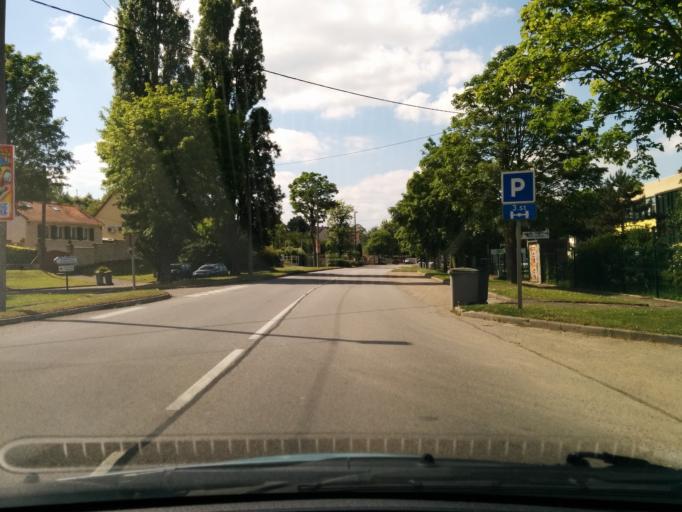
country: FR
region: Haute-Normandie
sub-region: Departement de l'Eure
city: Vernon
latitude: 49.0829
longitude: 1.5021
